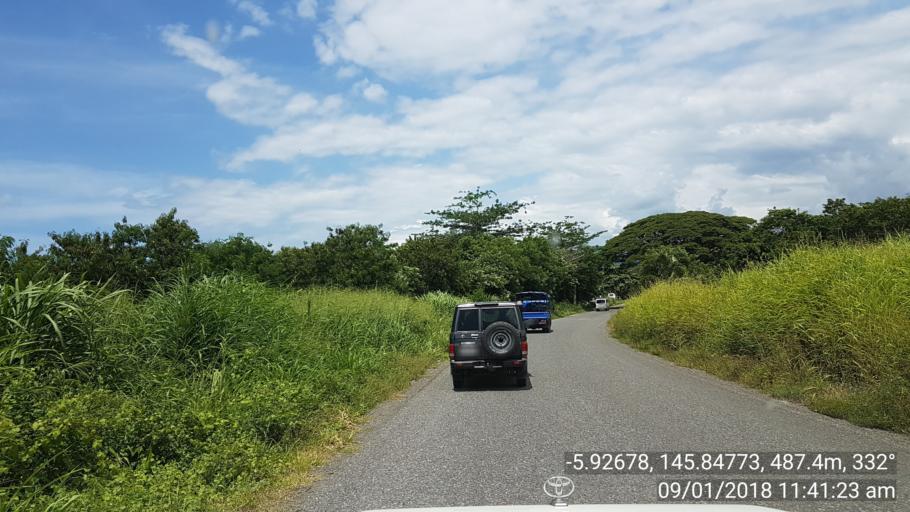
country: PG
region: Eastern Highlands
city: Kainantu
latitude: -5.9262
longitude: 145.8473
